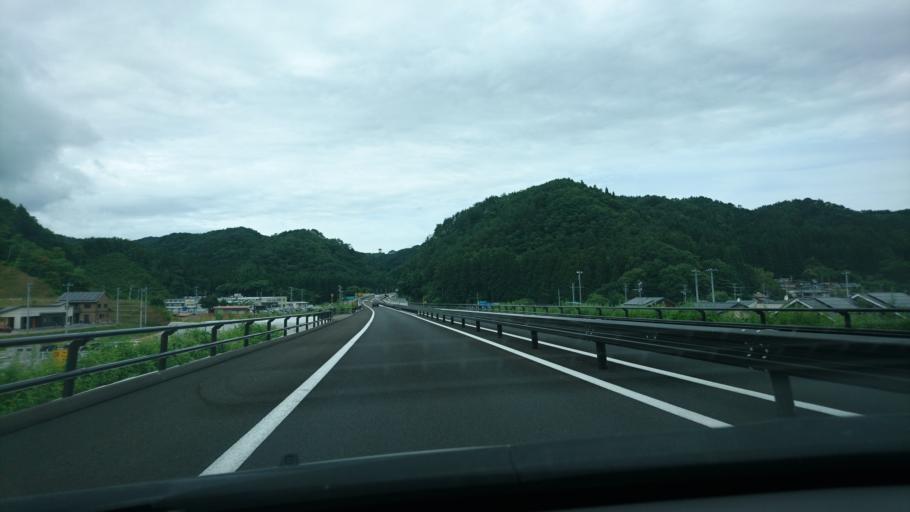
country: JP
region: Iwate
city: Miyako
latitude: 39.8405
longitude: 141.9569
